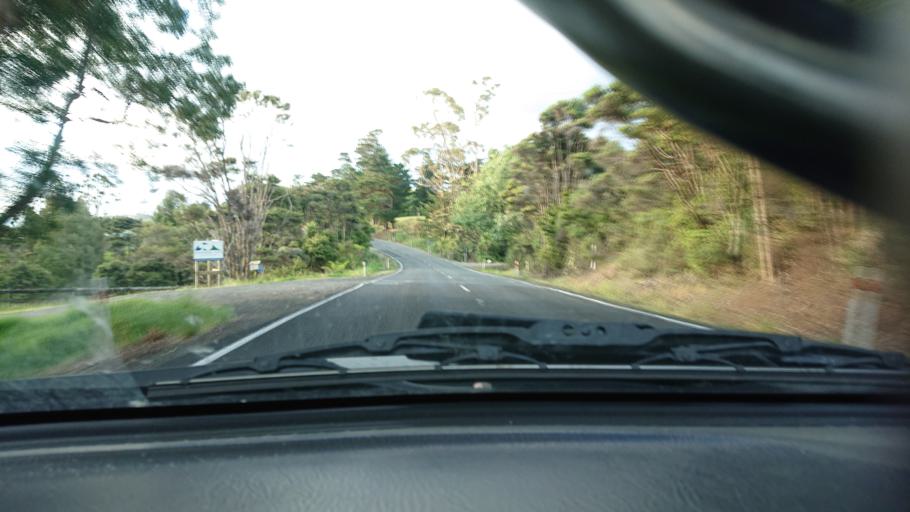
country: NZ
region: Auckland
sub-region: Auckland
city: Parakai
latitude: -36.5421
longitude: 174.4589
